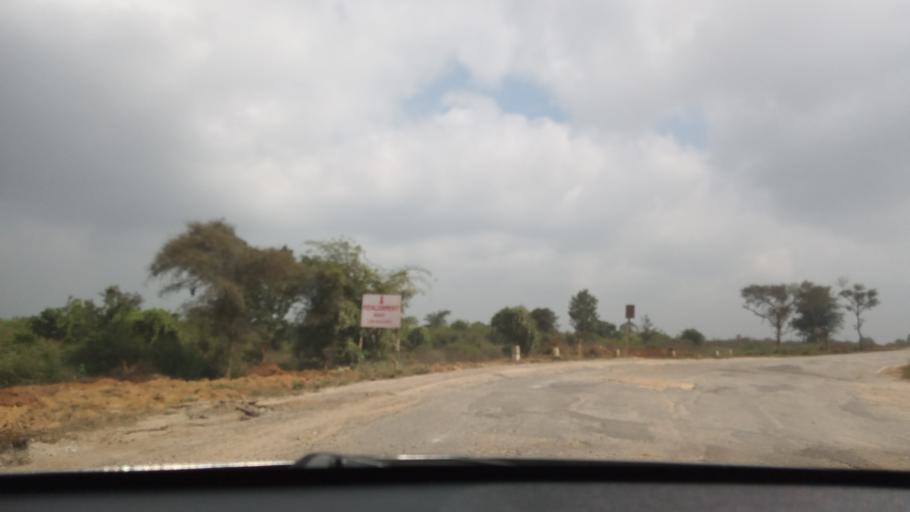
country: IN
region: Karnataka
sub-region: Kolar
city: Srinivaspur
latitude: 13.4404
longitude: 78.2271
